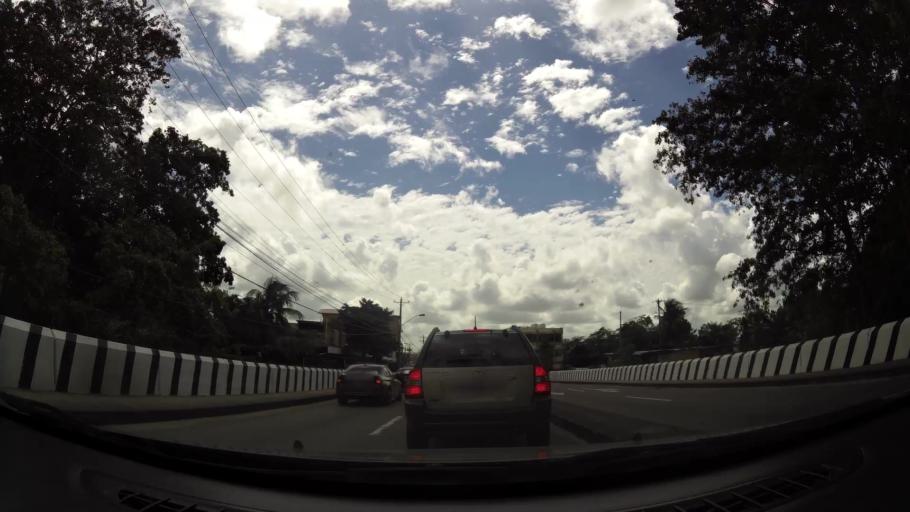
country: TT
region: City of San Fernando
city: Marabella
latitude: 10.3093
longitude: -61.4524
